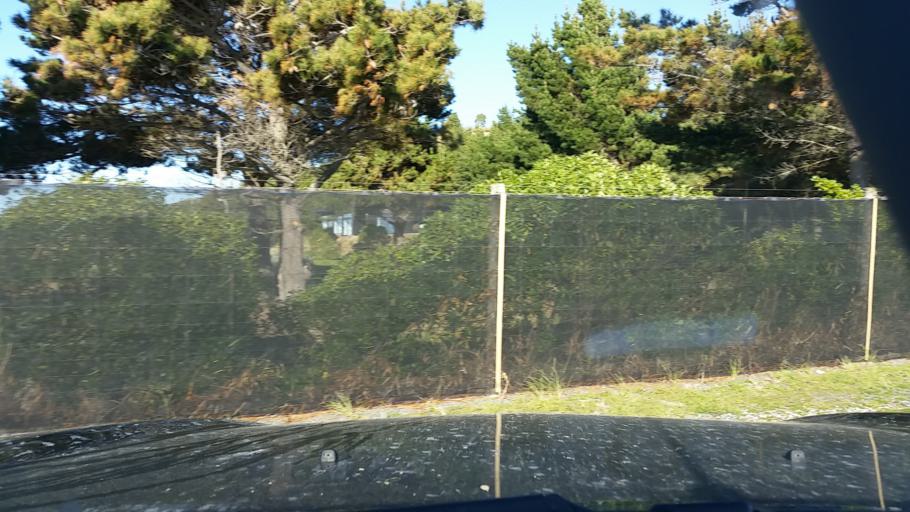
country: NZ
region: Marlborough
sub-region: Marlborough District
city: Blenheim
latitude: -41.6646
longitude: 174.1583
